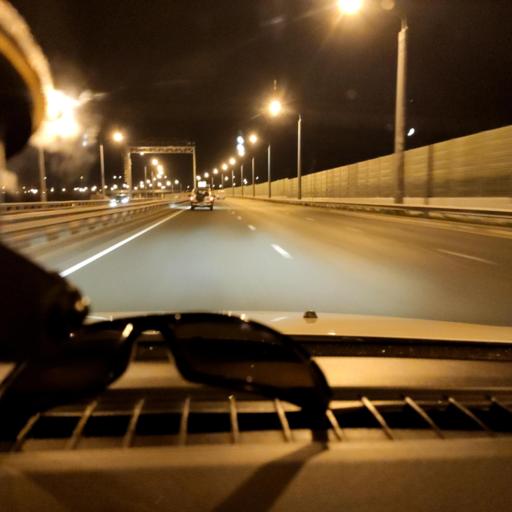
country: RU
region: Samara
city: Samara
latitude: 53.1693
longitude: 50.0858
